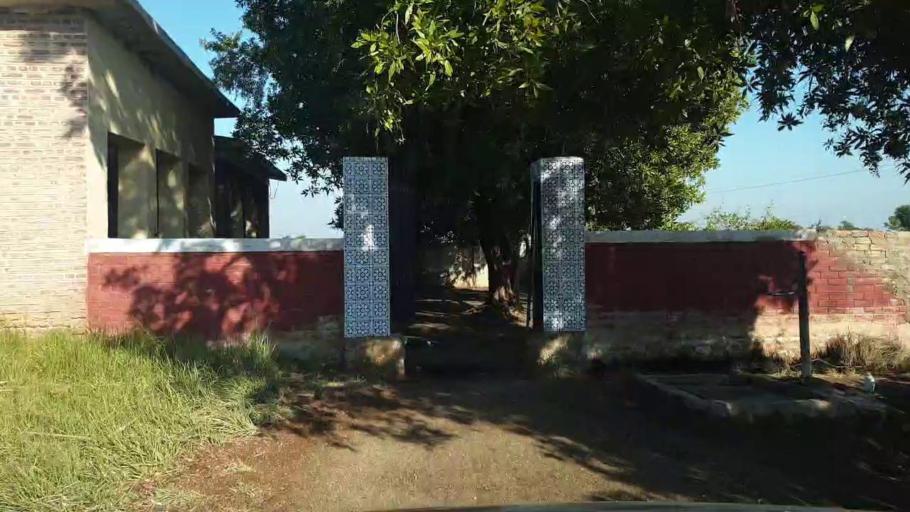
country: PK
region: Sindh
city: Shahdadpur
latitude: 25.9171
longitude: 68.5332
